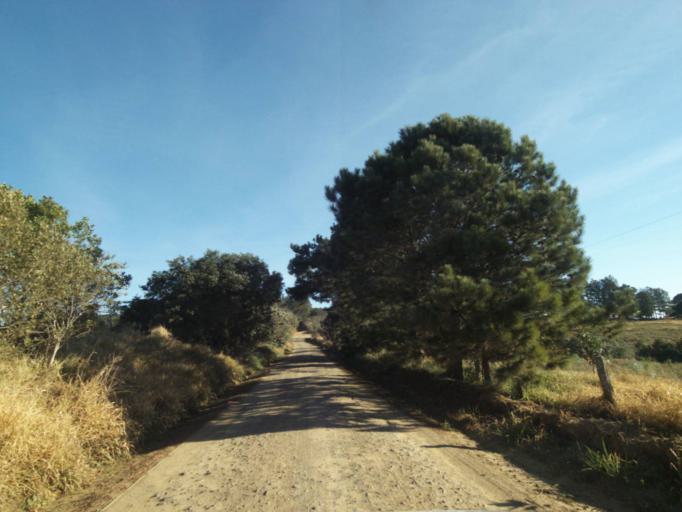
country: BR
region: Parana
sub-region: Tibagi
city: Tibagi
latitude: -24.5467
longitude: -50.6186
